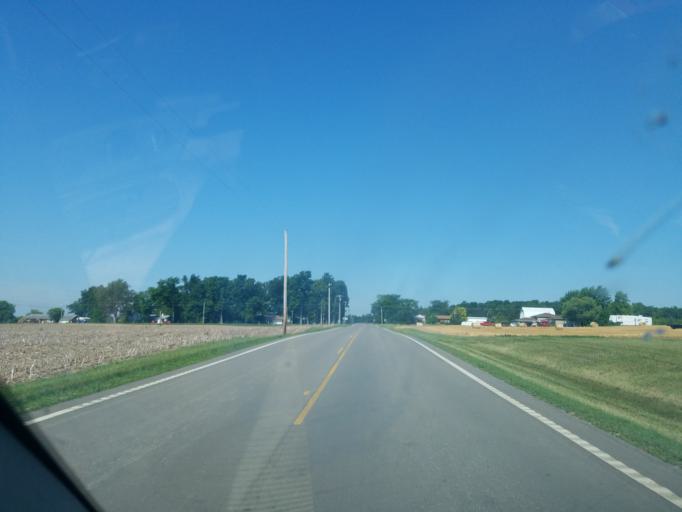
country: US
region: Ohio
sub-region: Logan County
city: Northwood
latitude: 40.4521
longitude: -83.7564
